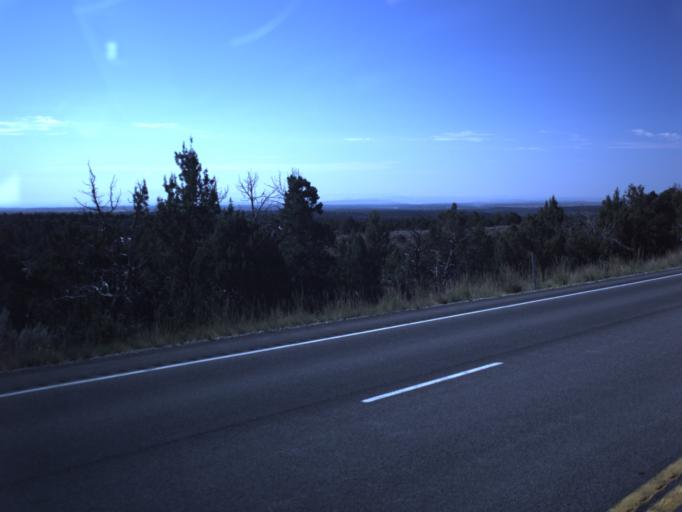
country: US
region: Utah
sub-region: San Juan County
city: Blanding
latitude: 37.7028
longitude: -109.4259
